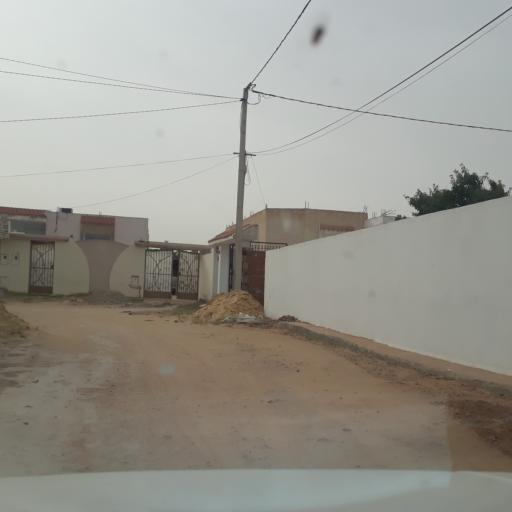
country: TN
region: Safaqis
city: Al Qarmadah
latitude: 34.8272
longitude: 10.7757
